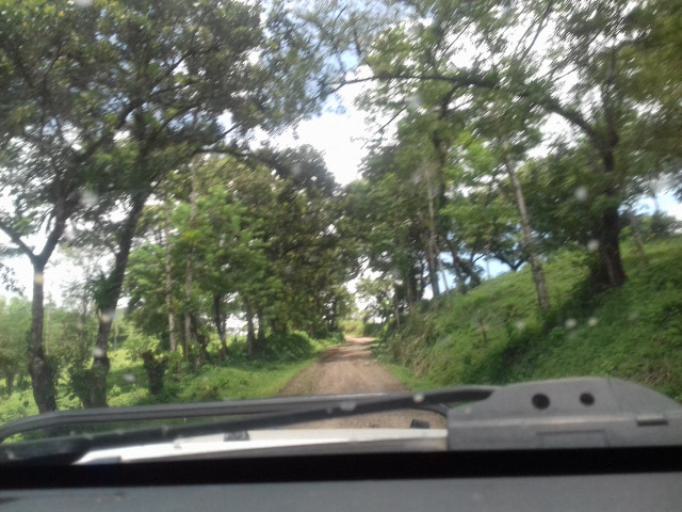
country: NI
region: Matagalpa
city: Rio Blanco
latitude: 12.9790
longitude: -85.3715
